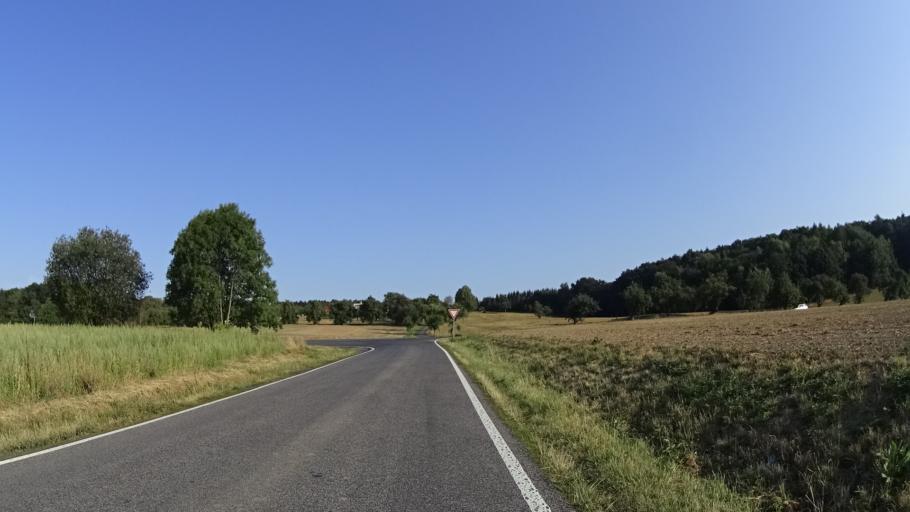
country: CZ
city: Ohrazenice
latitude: 50.6200
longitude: 15.1235
